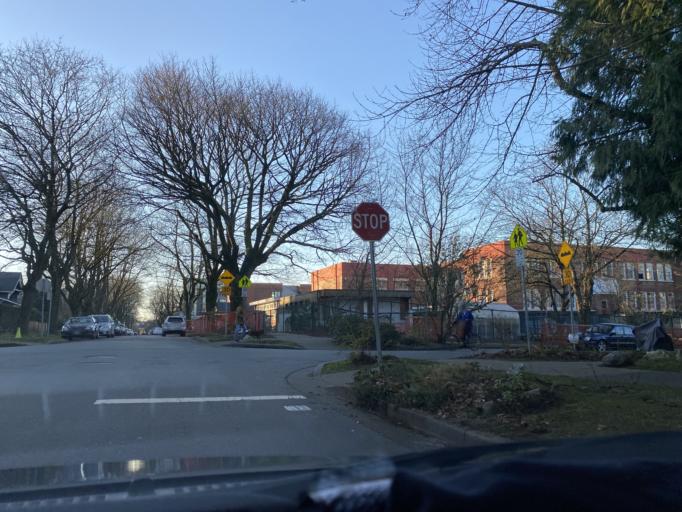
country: CA
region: British Columbia
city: West End
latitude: 49.2619
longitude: -123.1480
